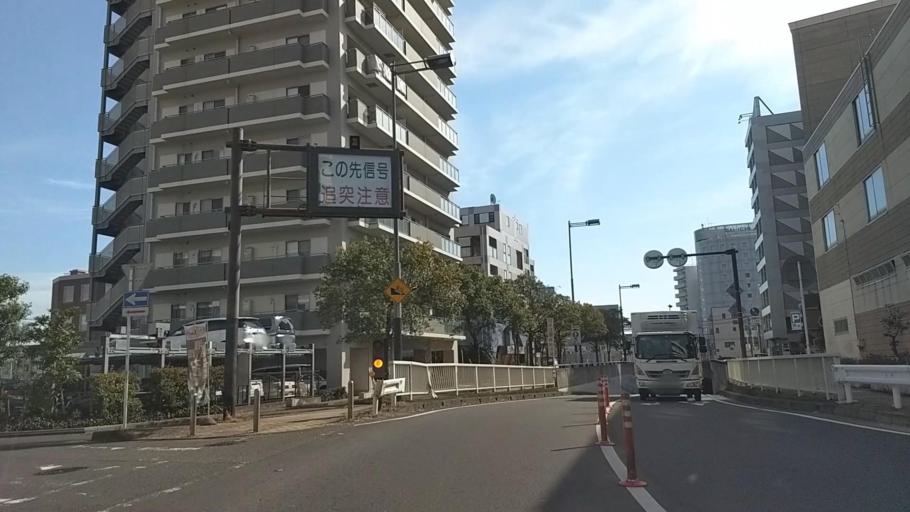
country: JP
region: Kanagawa
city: Fujisawa
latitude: 35.3384
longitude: 139.4493
